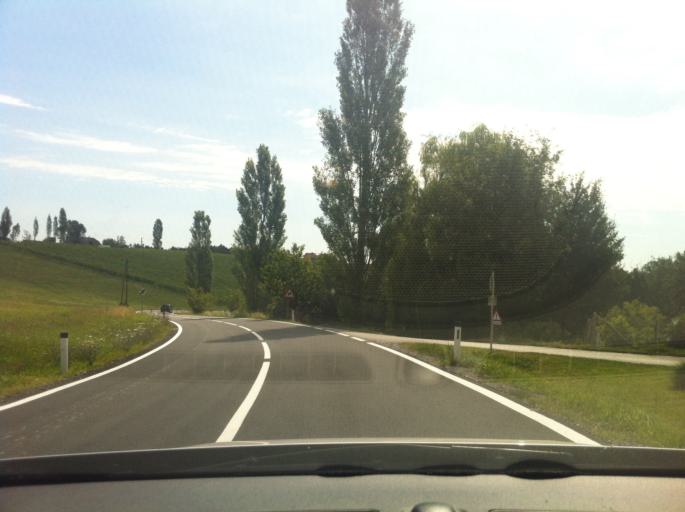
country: AT
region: Styria
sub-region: Politischer Bezirk Hartberg-Fuerstenfeld
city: Stubenberg
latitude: 47.2202
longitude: 15.8147
